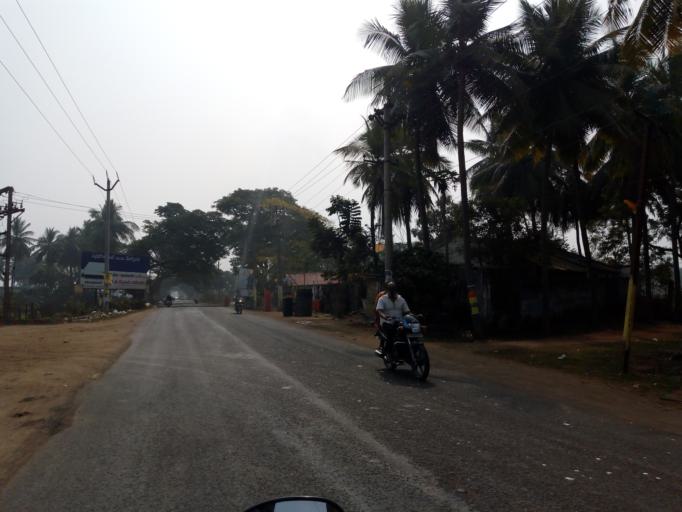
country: IN
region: Andhra Pradesh
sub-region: West Godavari
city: Bhimavaram
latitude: 16.5815
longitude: 81.4740
